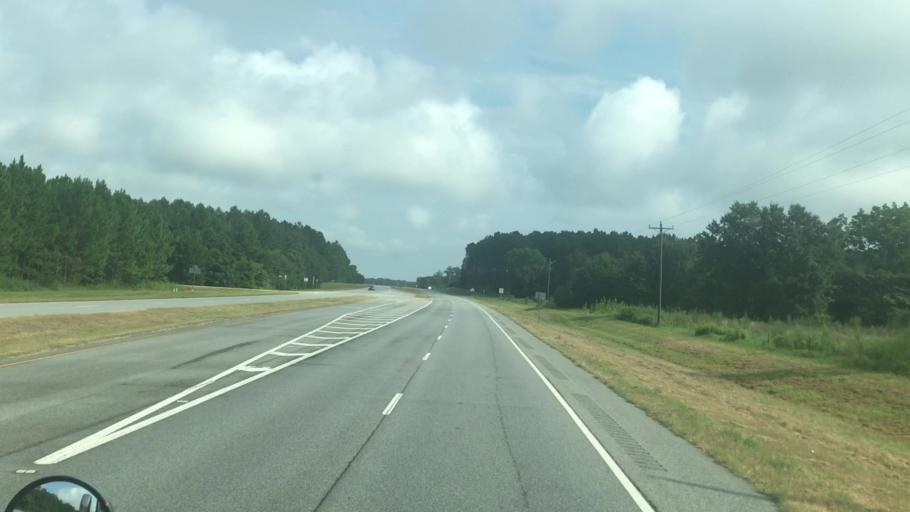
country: US
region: Georgia
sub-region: Miller County
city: Colquitt
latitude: 31.2262
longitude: -84.7807
